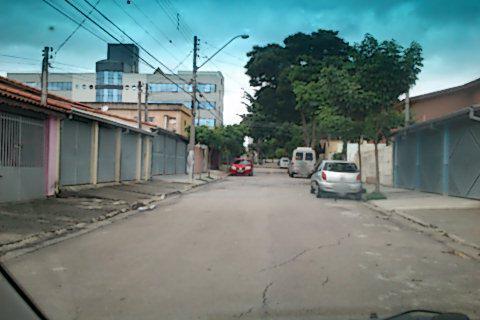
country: BR
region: Sao Paulo
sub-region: Sao Jose Dos Campos
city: Sao Jose dos Campos
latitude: -23.2409
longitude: -45.8859
